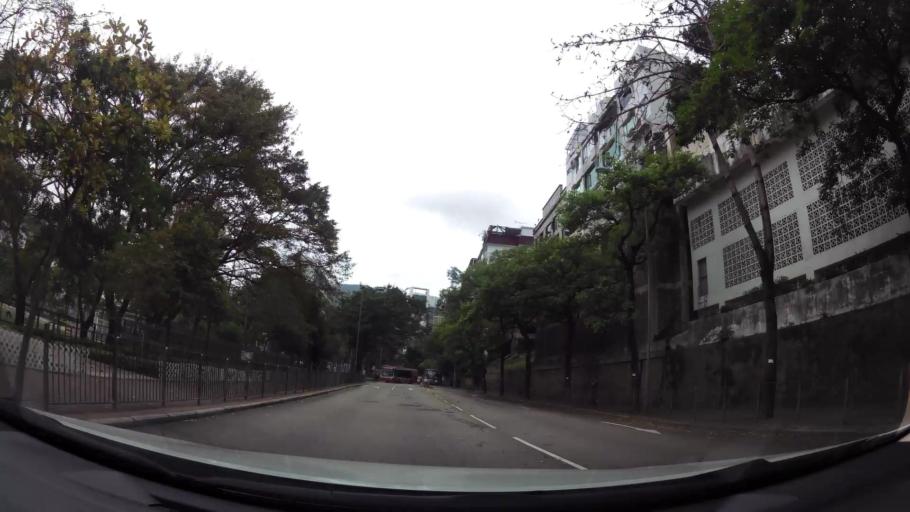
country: HK
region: Sham Shui Po
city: Sham Shui Po
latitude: 22.3288
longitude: 114.1720
